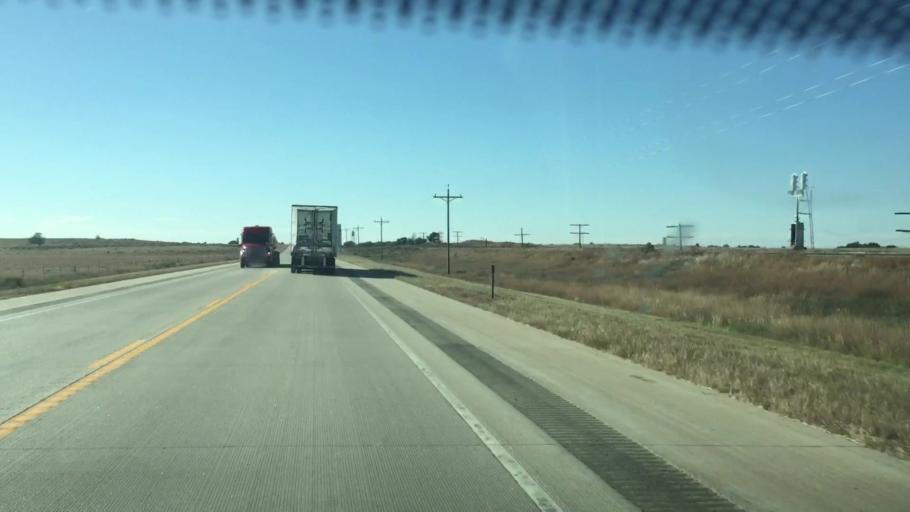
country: US
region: Colorado
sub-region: Kiowa County
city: Eads
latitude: 38.4759
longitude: -102.7584
